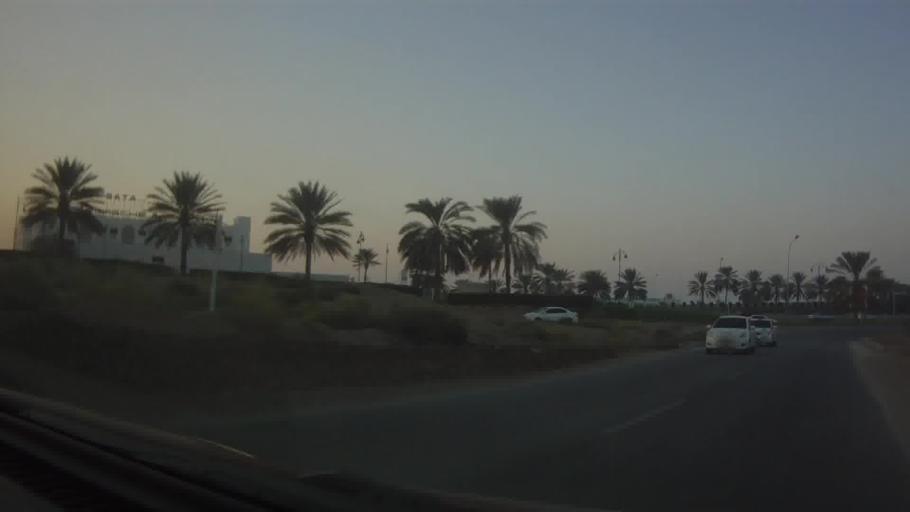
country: OM
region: Muhafazat Masqat
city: Bawshar
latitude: 23.5941
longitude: 58.4124
